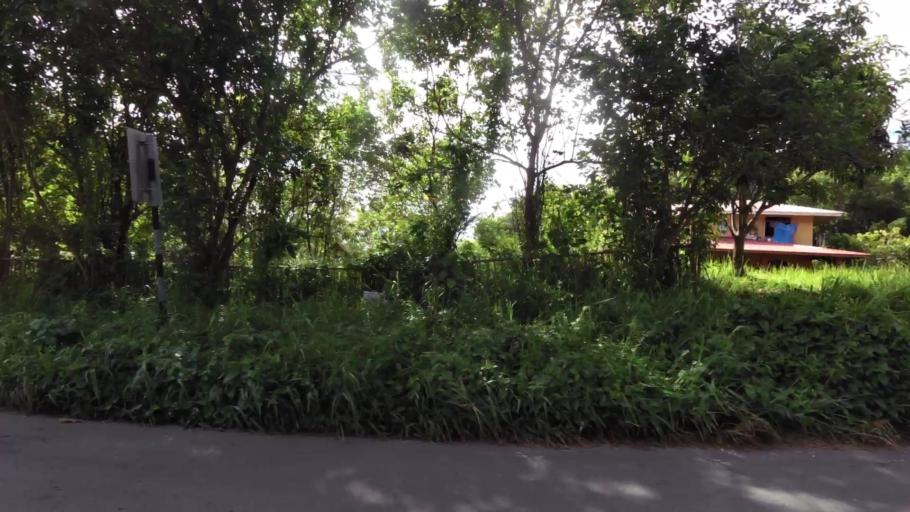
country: BN
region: Brunei and Muara
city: Bandar Seri Begawan
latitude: 4.9220
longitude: 114.8988
